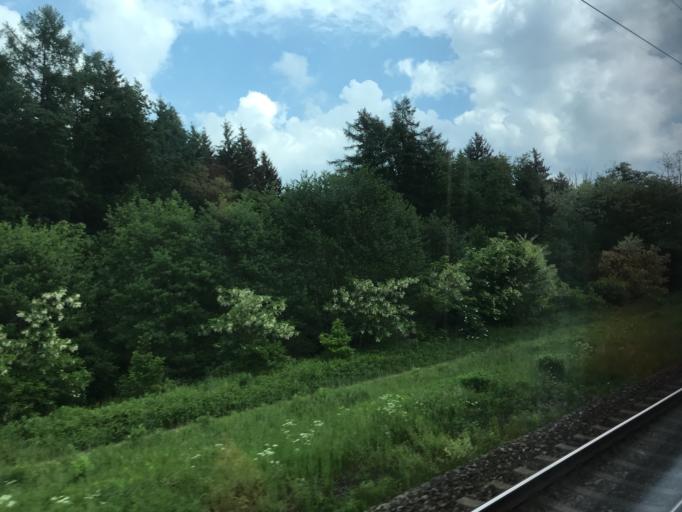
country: DE
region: Bavaria
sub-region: Swabia
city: Rosshaupten
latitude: 48.3950
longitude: 10.4834
